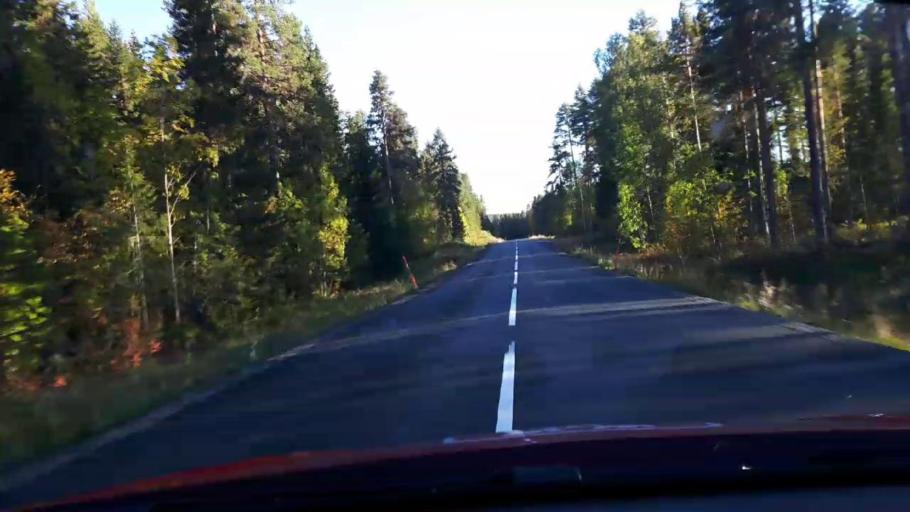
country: SE
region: Jaemtland
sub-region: OEstersunds Kommun
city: Lit
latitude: 63.5302
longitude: 14.8455
